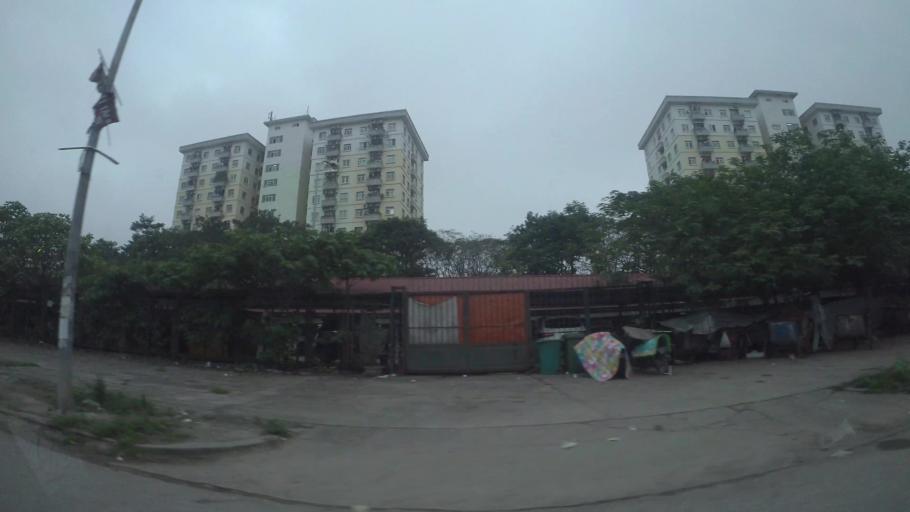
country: VN
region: Ha Noi
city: Thanh Xuan
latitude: 20.9862
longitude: 105.8273
